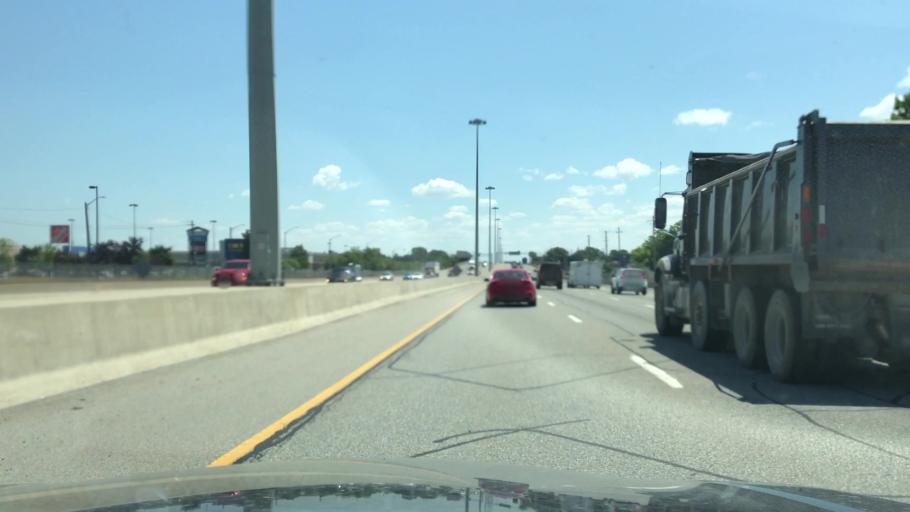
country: CA
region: Ontario
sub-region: Regional Municipality of Niagara
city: St. Catharines
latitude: 43.1755
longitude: -79.2473
